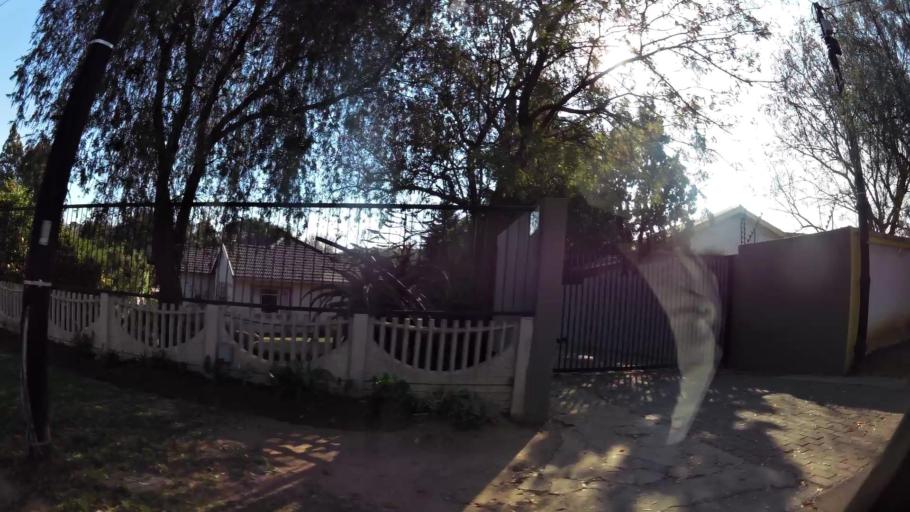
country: ZA
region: Gauteng
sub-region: City of Johannesburg Metropolitan Municipality
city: Roodepoort
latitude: -26.0996
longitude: 27.9683
